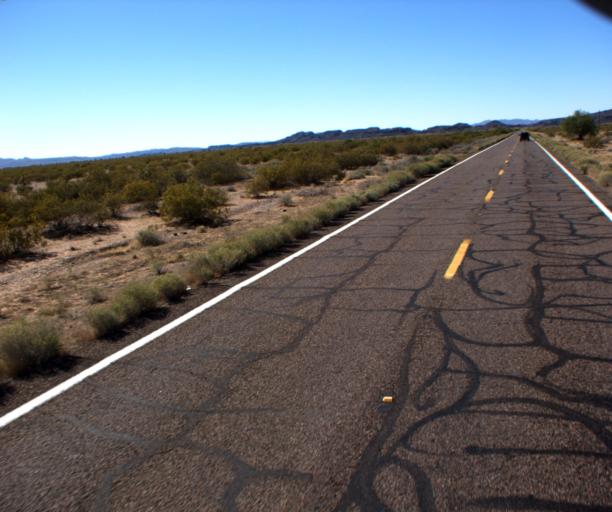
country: US
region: Arizona
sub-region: Pima County
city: Ajo
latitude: 32.5986
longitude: -112.8706
